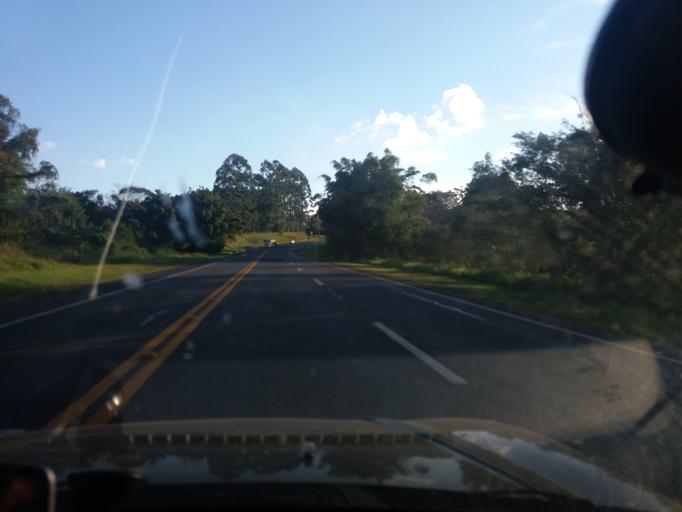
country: BR
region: Sao Paulo
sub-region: Buri
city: Buri
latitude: -23.9283
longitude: -48.6645
